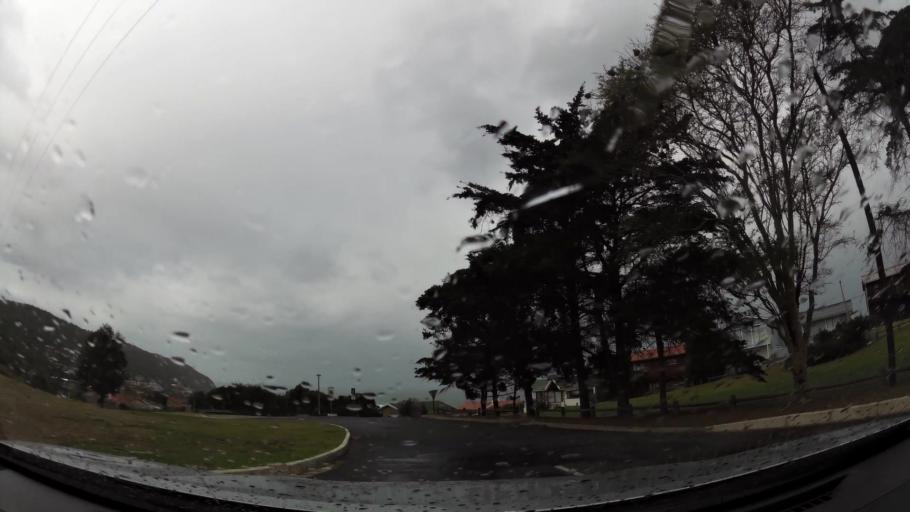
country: ZA
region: Western Cape
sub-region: Eden District Municipality
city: George
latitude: -34.0480
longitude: 22.3079
